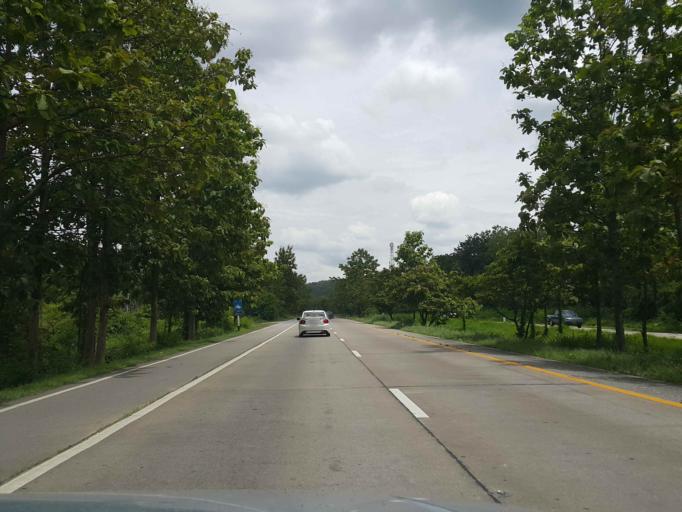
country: TH
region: Lamphun
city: Mae Tha
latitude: 18.5143
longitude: 99.0939
